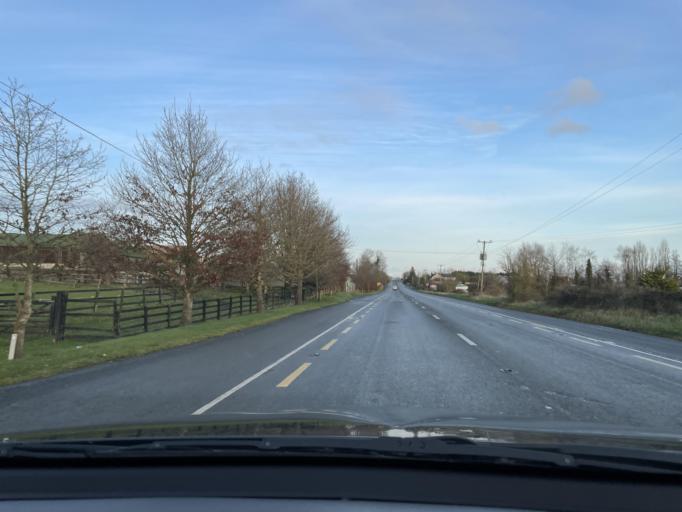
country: IE
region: Leinster
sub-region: Kilkenny
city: Thomastown
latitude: 52.6474
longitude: -7.1181
